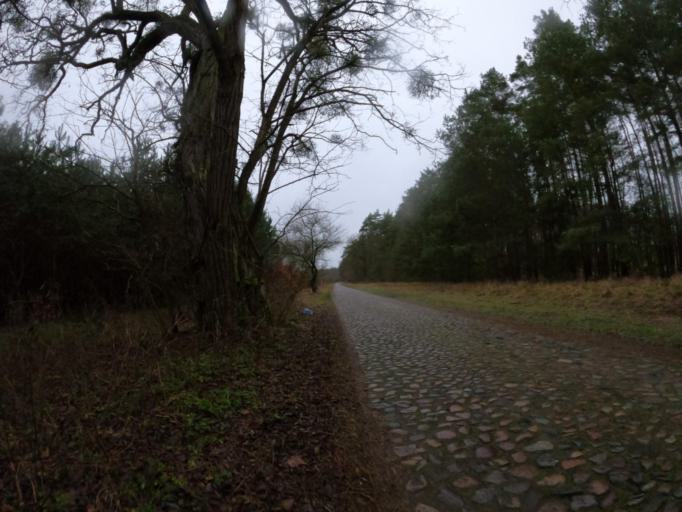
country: PL
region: West Pomeranian Voivodeship
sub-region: Powiat mysliborski
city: Debno
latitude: 52.8097
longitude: 14.7357
